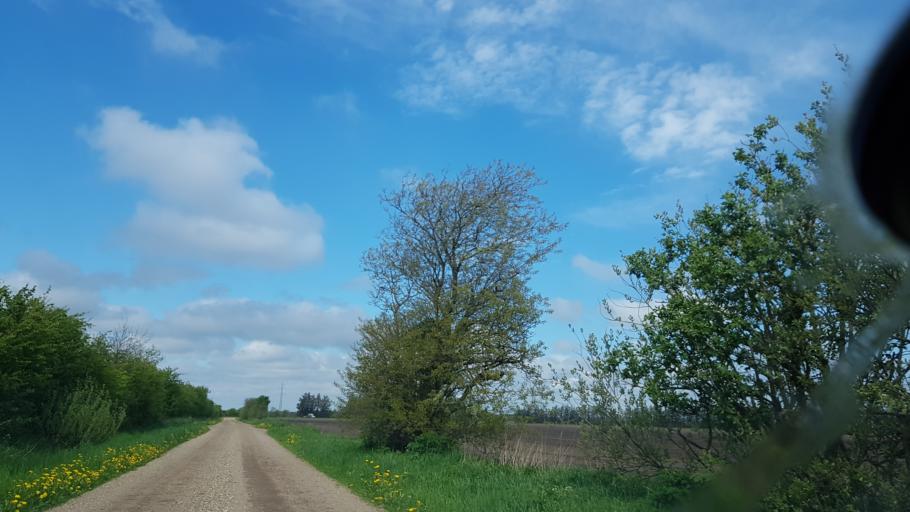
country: DK
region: South Denmark
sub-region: Tonder Kommune
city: Sherrebek
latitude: 55.0817
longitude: 8.8392
